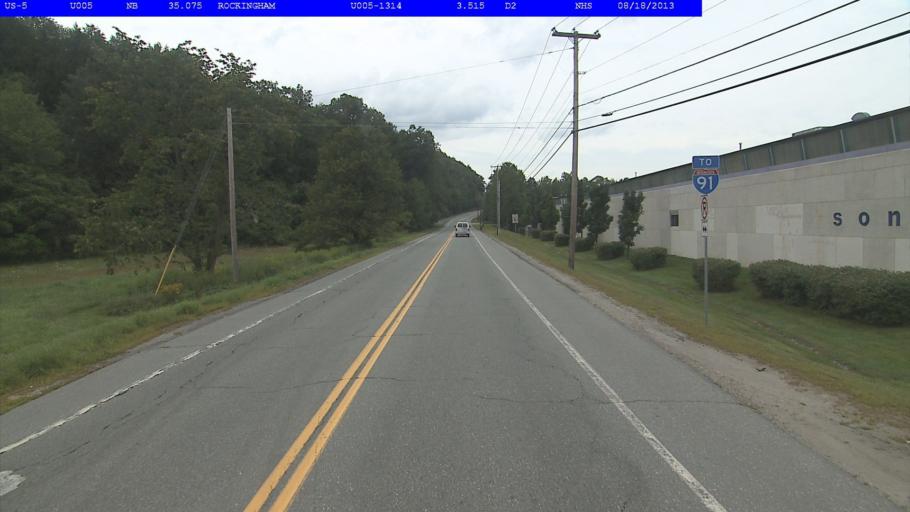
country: US
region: Vermont
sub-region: Windham County
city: Rockingham
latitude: 43.1717
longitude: -72.4585
